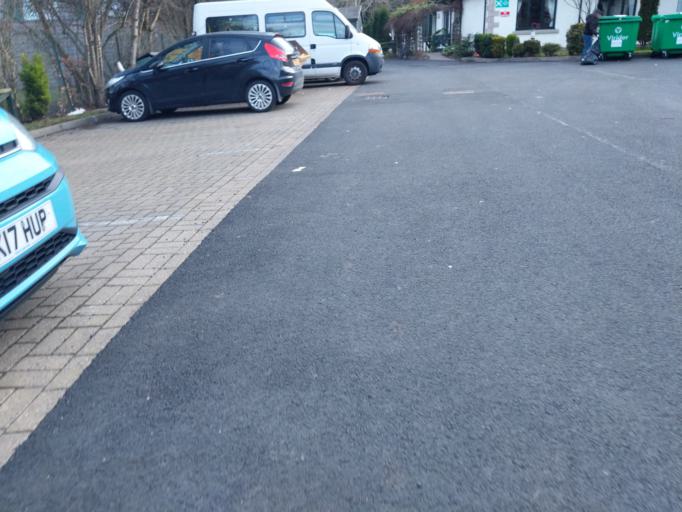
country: GB
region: Scotland
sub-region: Edinburgh
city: Colinton
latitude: 55.9554
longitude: -3.2631
